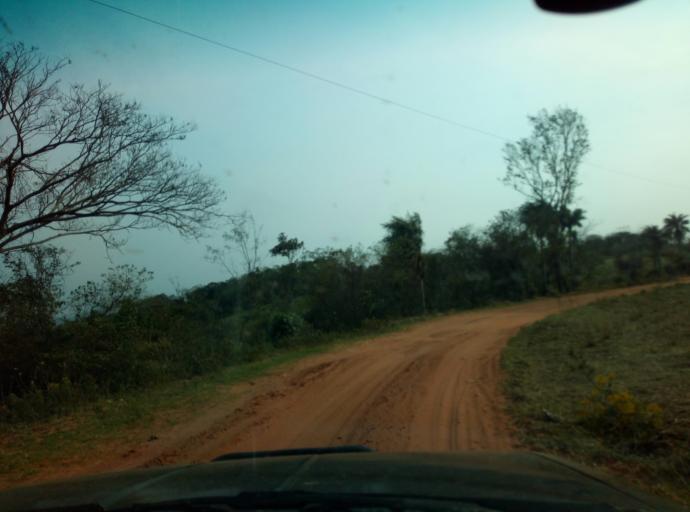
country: PY
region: Caaguazu
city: San Joaquin
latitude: -25.1528
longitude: -56.1053
